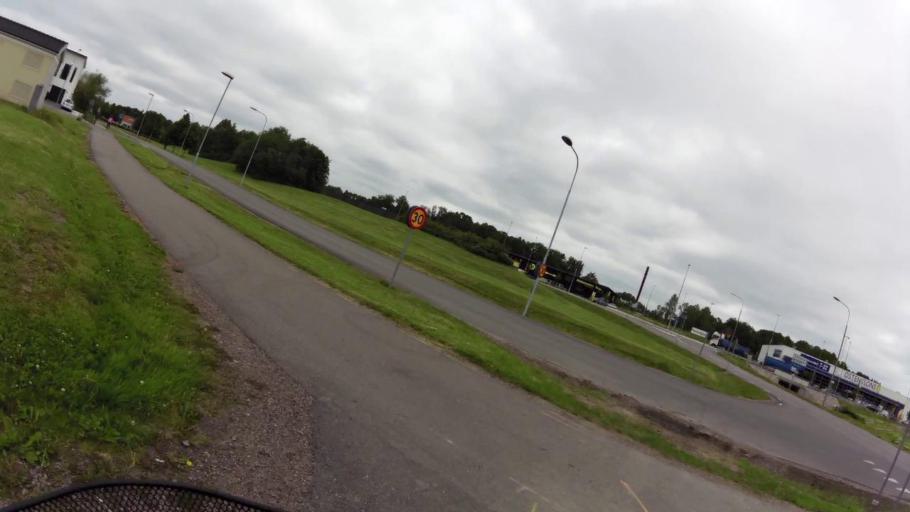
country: SE
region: OEstergoetland
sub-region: Linkopings Kommun
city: Sturefors
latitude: 58.3669
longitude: 15.6900
